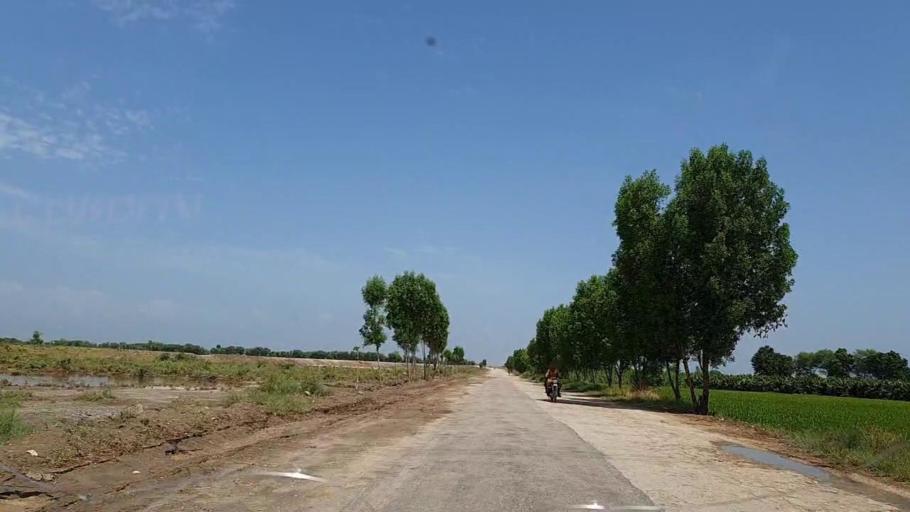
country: PK
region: Sindh
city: Naushahro Firoz
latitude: 26.8264
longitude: 68.1517
